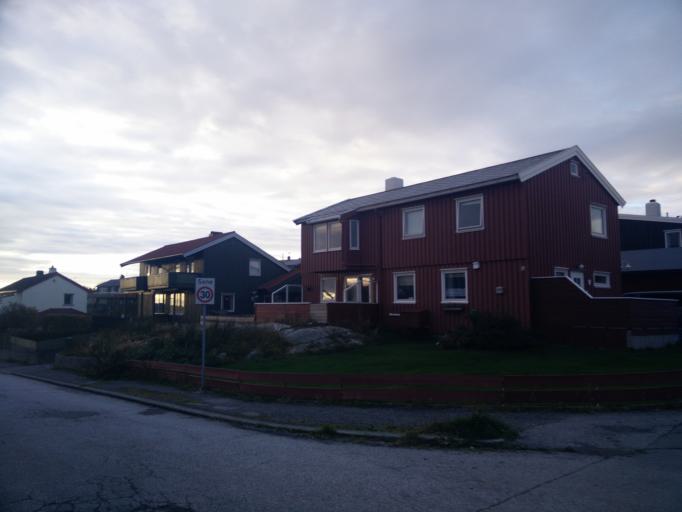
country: NO
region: More og Romsdal
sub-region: Kristiansund
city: Kristiansund
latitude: 63.1238
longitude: 7.7147
